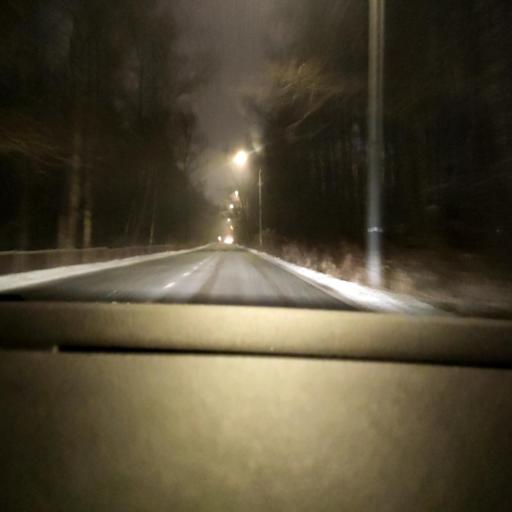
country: RU
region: Moskovskaya
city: Bogorodskoye
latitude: 55.8306
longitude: 37.7458
